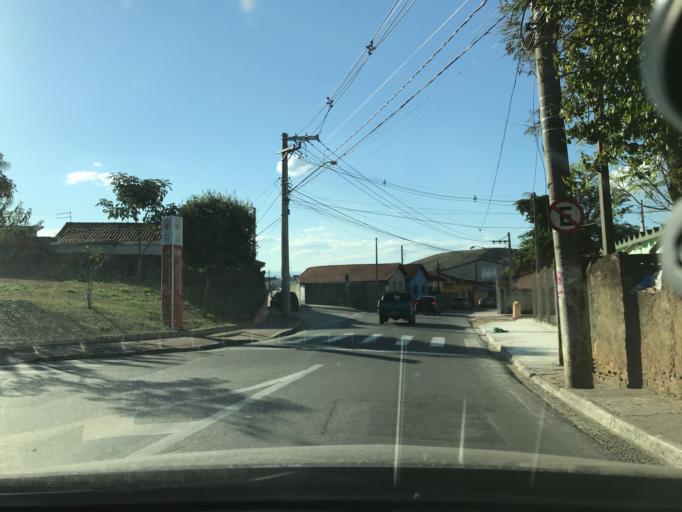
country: BR
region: Sao Paulo
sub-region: Sao Jose Dos Campos
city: Sao Jose dos Campos
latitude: -23.1542
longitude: -45.9014
